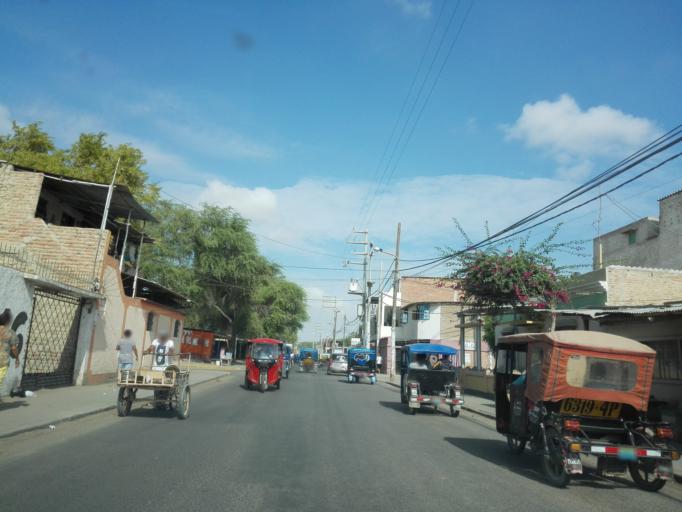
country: PE
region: Piura
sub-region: Provincia de Piura
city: Piura
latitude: -5.1943
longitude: -80.6433
